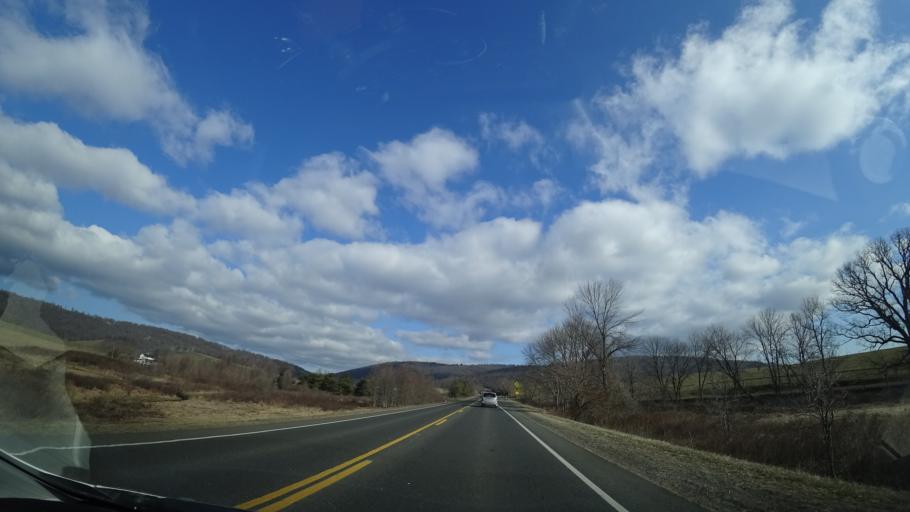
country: US
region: Virginia
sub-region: Warren County
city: Shenandoah Farms
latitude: 38.9918
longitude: -77.9487
